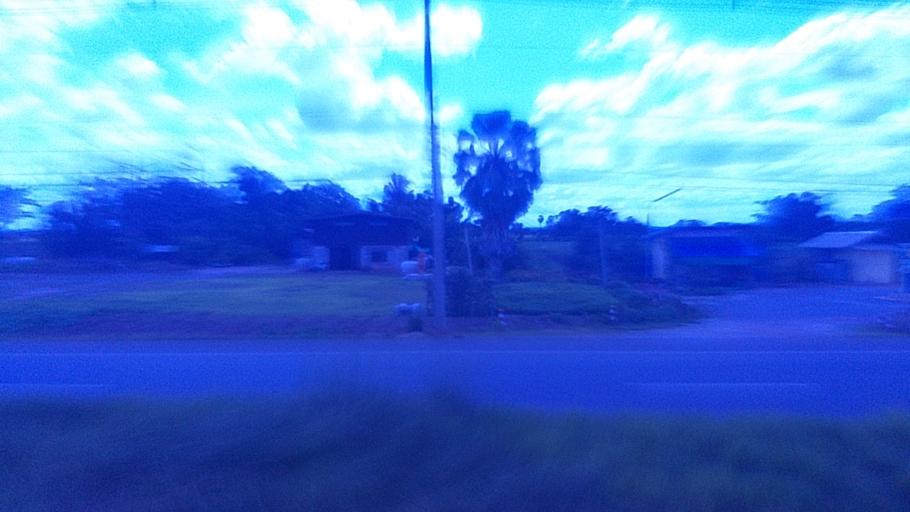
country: TH
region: Nakhon Ratchasima
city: Dan Khun Thot
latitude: 15.1021
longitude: 101.7213
